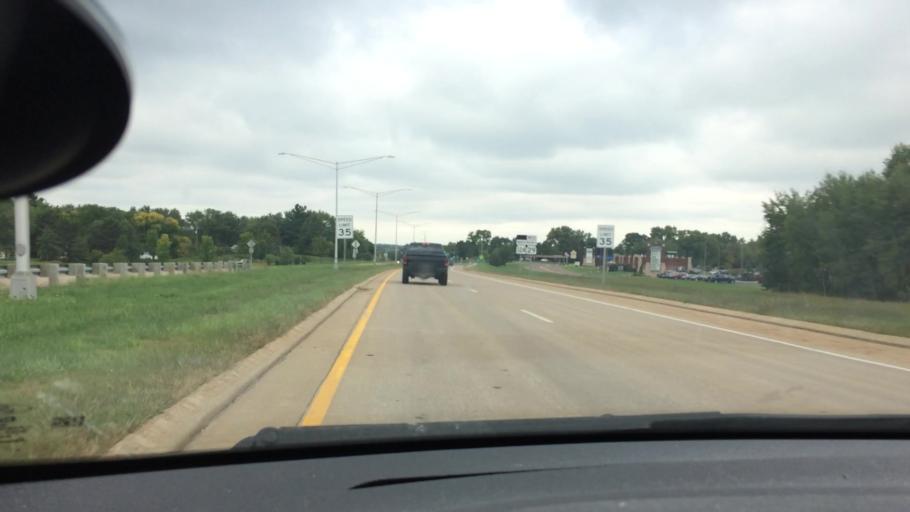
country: US
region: Wisconsin
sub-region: Chippewa County
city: Chippewa Falls
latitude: 44.9223
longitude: -91.3813
